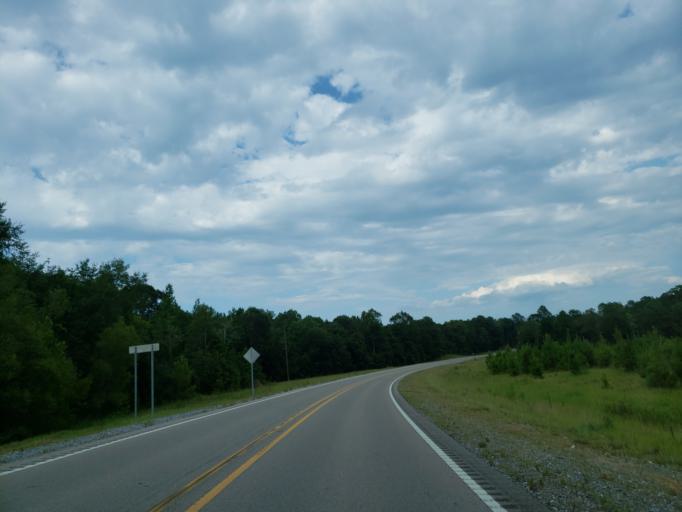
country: US
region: Mississippi
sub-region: Clarke County
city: Stonewall
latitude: 32.1782
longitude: -88.9249
